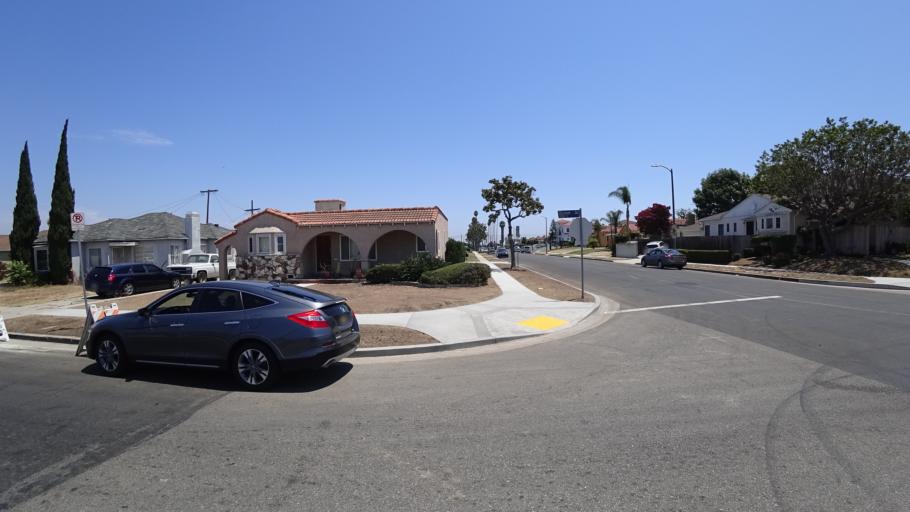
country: US
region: California
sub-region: Los Angeles County
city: Westmont
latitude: 33.9488
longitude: -118.3047
